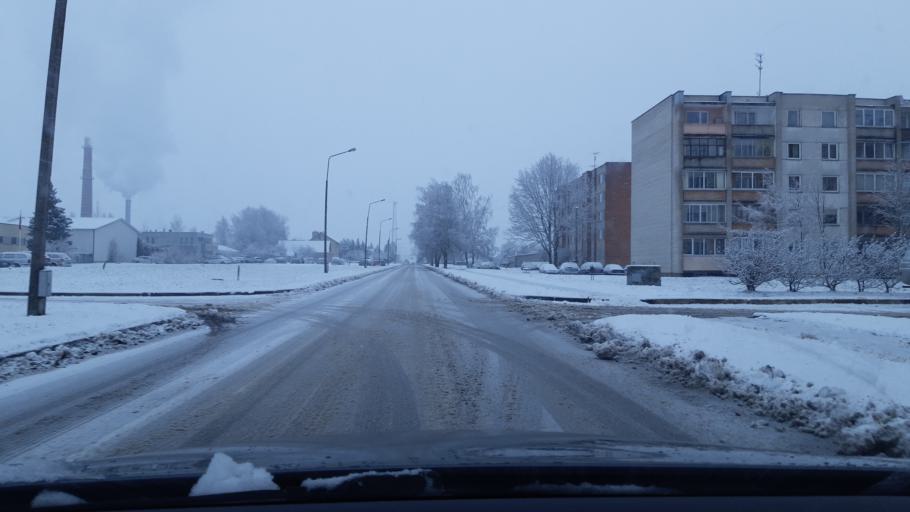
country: LT
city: Kaisiadorys
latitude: 54.8609
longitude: 24.4420
